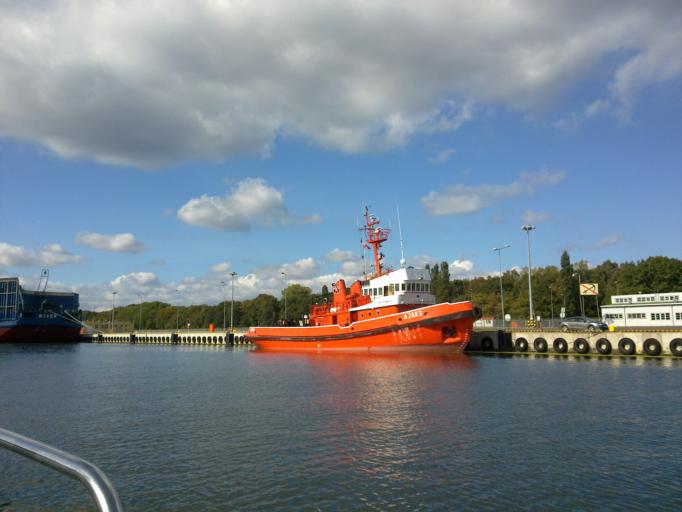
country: PL
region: Pomeranian Voivodeship
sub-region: Gdansk
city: Gdansk
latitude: 54.4036
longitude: 18.6778
